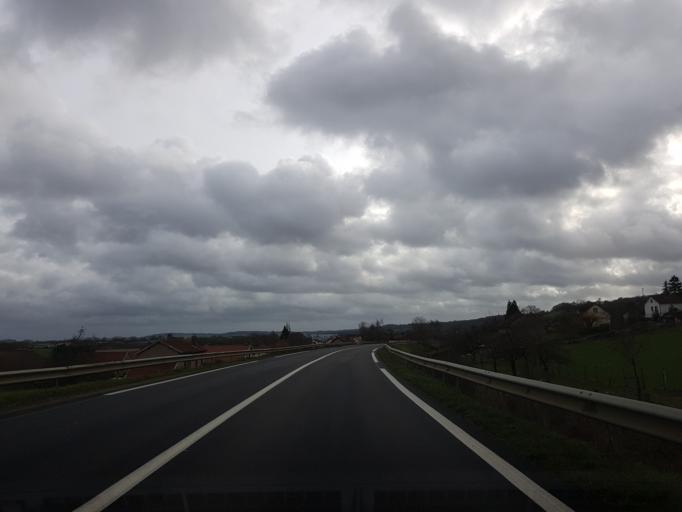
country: FR
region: Champagne-Ardenne
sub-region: Departement de la Haute-Marne
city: Langres
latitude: 47.8676
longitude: 5.3421
